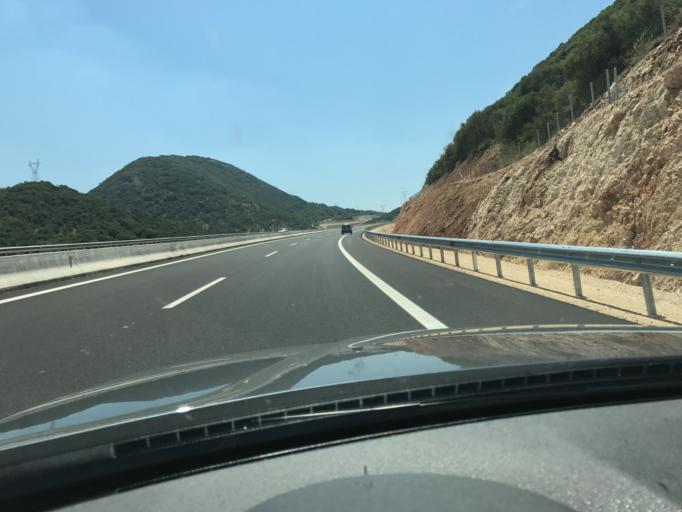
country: GR
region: Epirus
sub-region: Nomos Ioanninon
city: Agia Kyriaki
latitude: 39.5128
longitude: 20.8883
